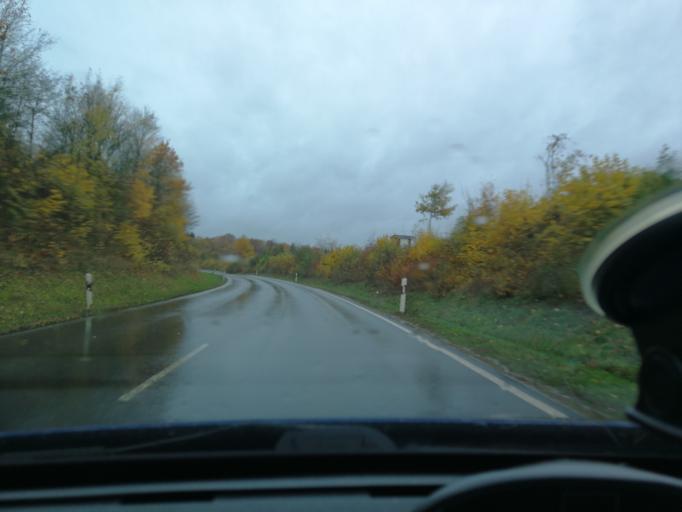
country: DE
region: Rheinland-Pfalz
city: Klausen
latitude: 49.9087
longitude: 6.8806
